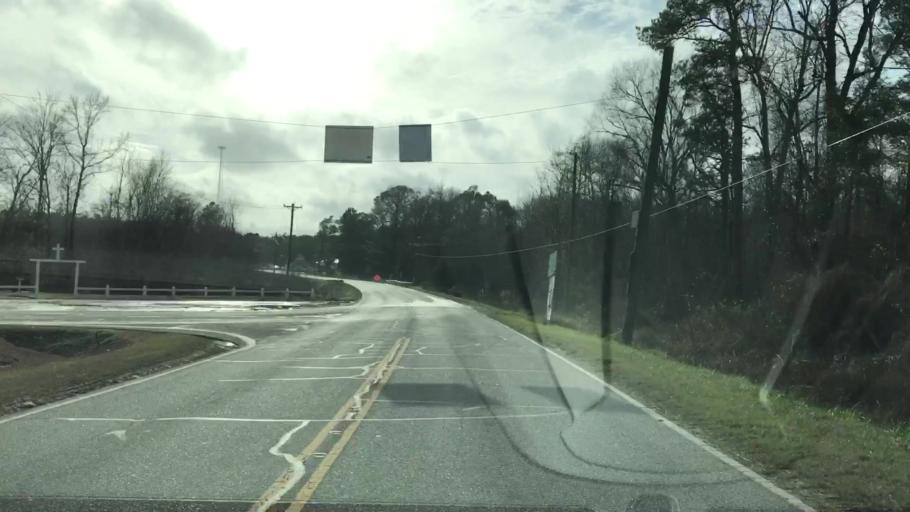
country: US
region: South Carolina
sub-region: Williamsburg County
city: Andrews
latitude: 33.3608
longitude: -79.6533
